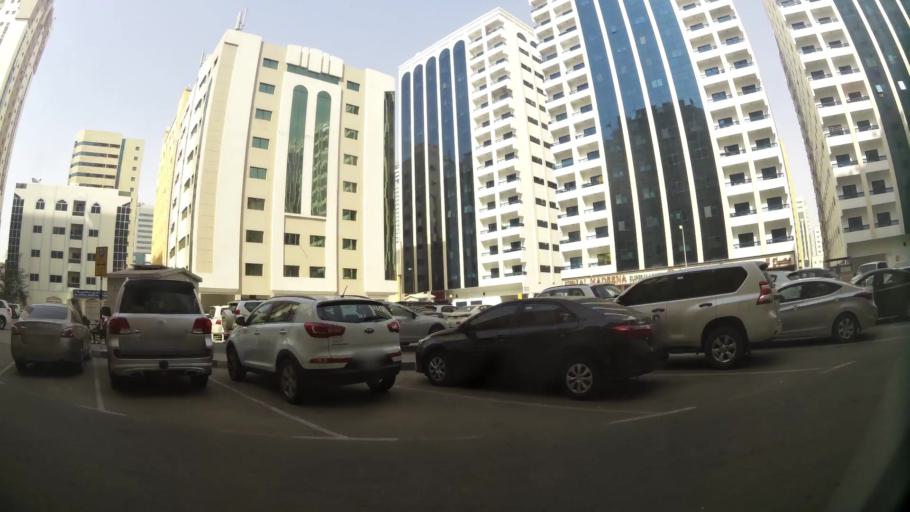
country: AE
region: Ash Shariqah
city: Sharjah
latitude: 25.3452
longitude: 55.3890
